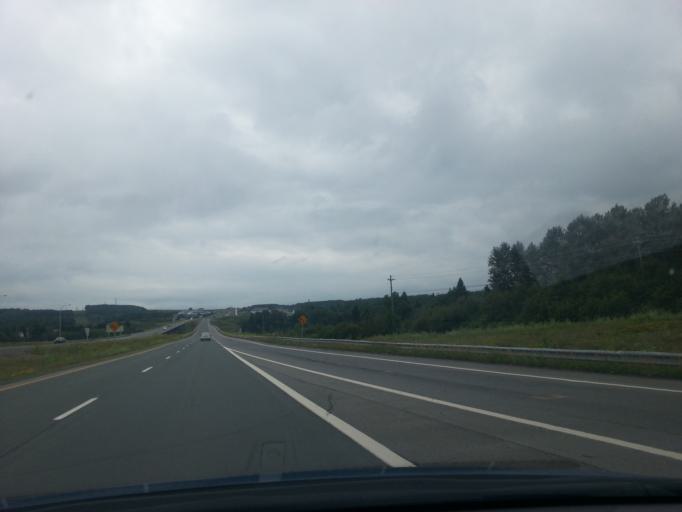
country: US
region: Maine
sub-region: Aroostook County
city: Limestone
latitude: 47.0628
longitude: -67.7646
